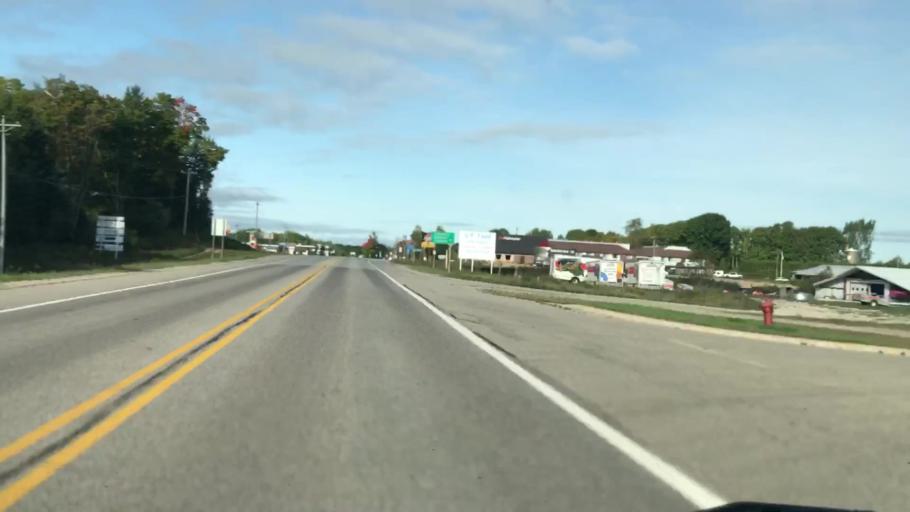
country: US
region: Michigan
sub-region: Luce County
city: Newberry
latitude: 46.3035
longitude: -85.5054
